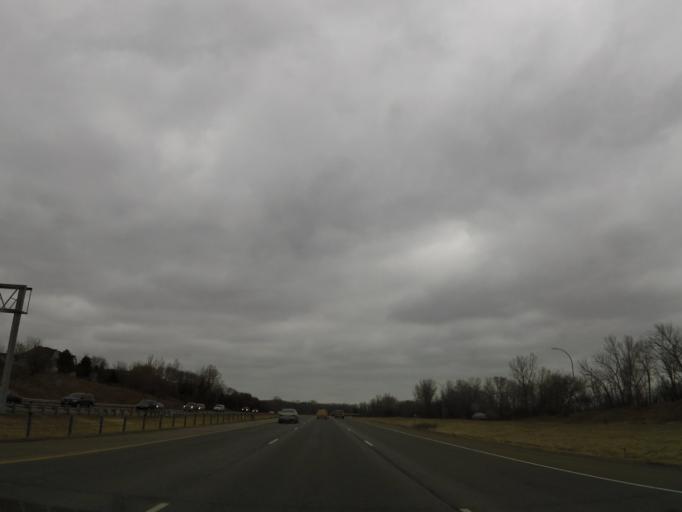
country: US
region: Minnesota
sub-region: Dakota County
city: Mendota Heights
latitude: 44.8669
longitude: -93.1447
